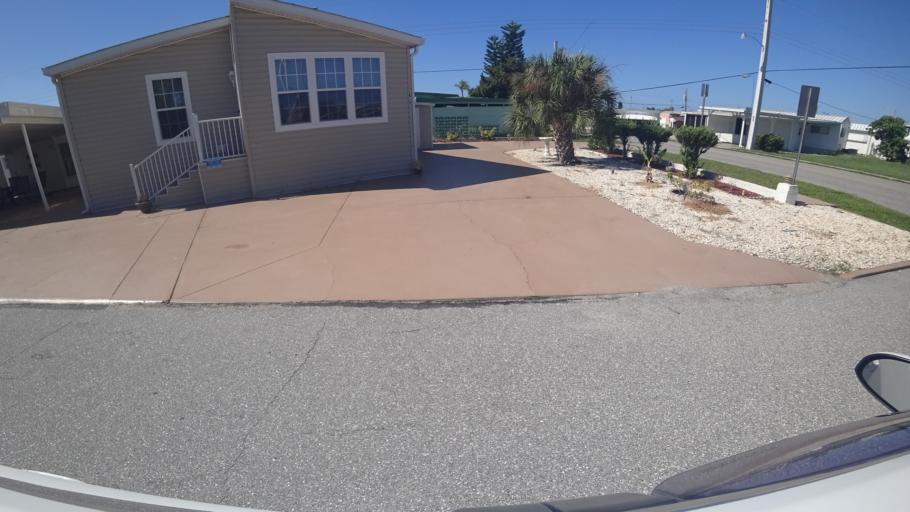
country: US
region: Florida
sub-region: Manatee County
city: Bayshore Gardens
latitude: 27.4209
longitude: -82.5804
